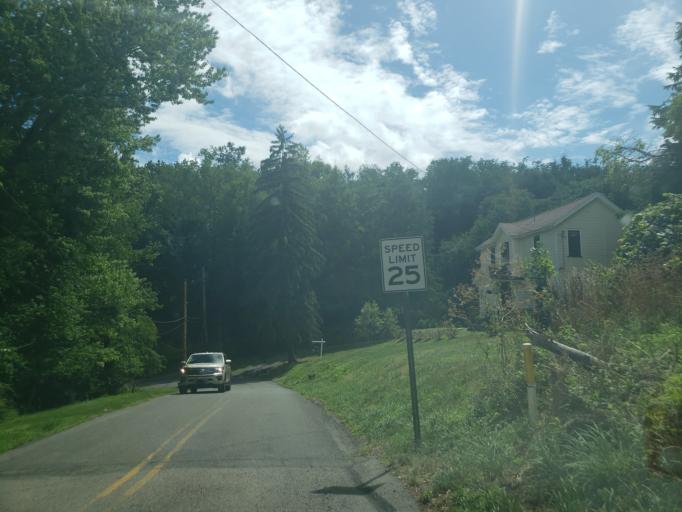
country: US
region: Pennsylvania
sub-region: Allegheny County
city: Coraopolis
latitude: 40.5251
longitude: -80.1417
